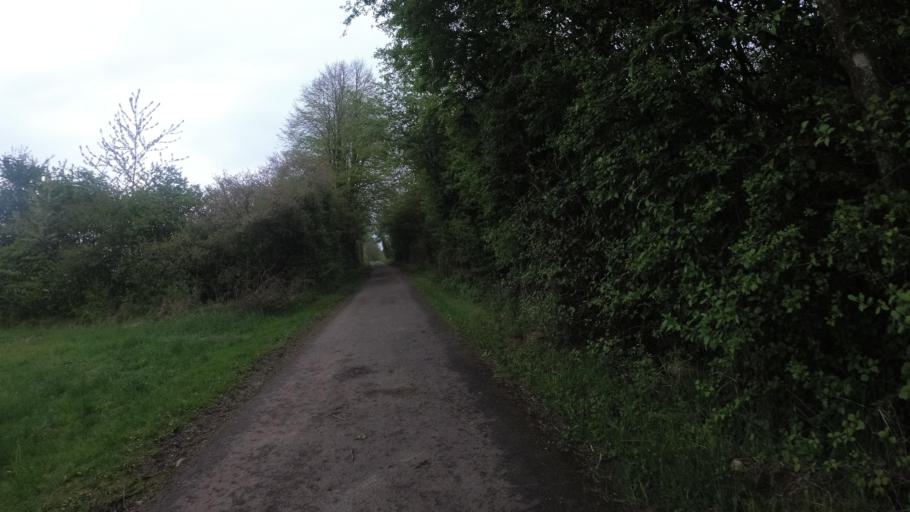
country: DE
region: Saarland
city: Rehlingen-Siersburg
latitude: 49.3239
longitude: 6.6508
